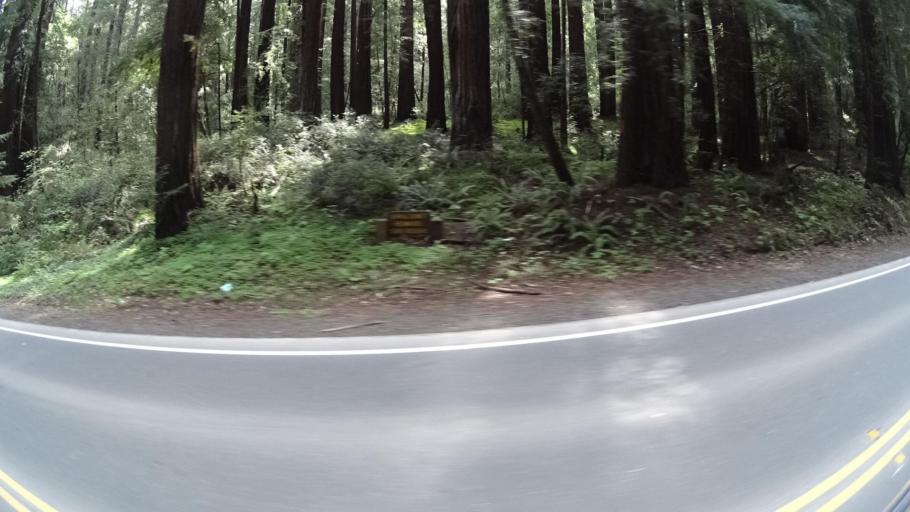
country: US
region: California
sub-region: Humboldt County
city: Redway
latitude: 40.1341
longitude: -123.8168
